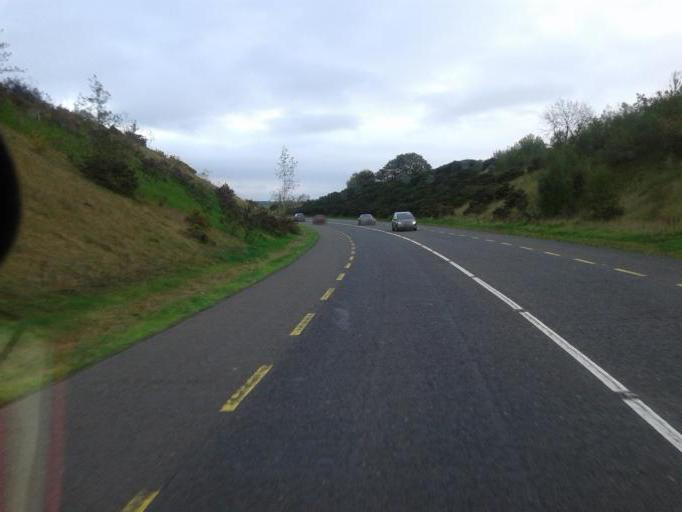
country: IE
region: Munster
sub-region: North Tipperary
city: Newport
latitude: 52.7600
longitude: -8.4197
